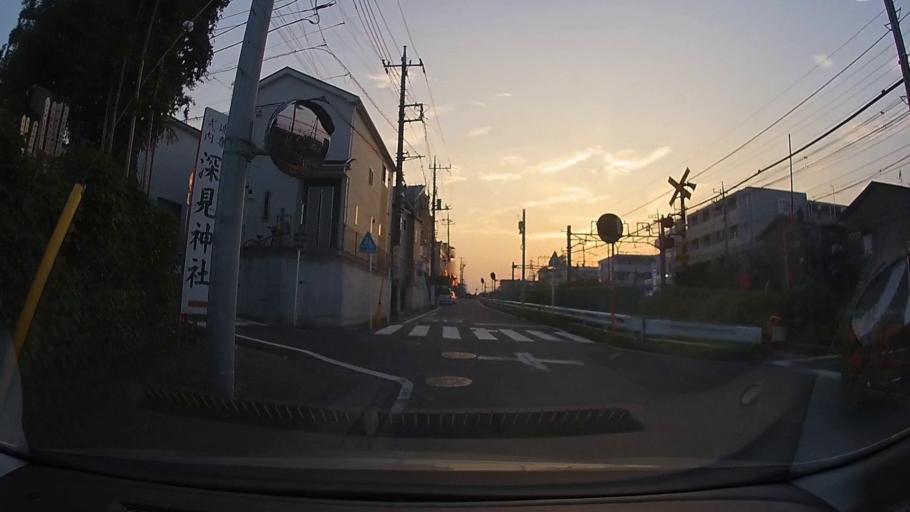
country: JP
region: Kanagawa
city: Minami-rinkan
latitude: 35.4695
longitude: 139.4719
